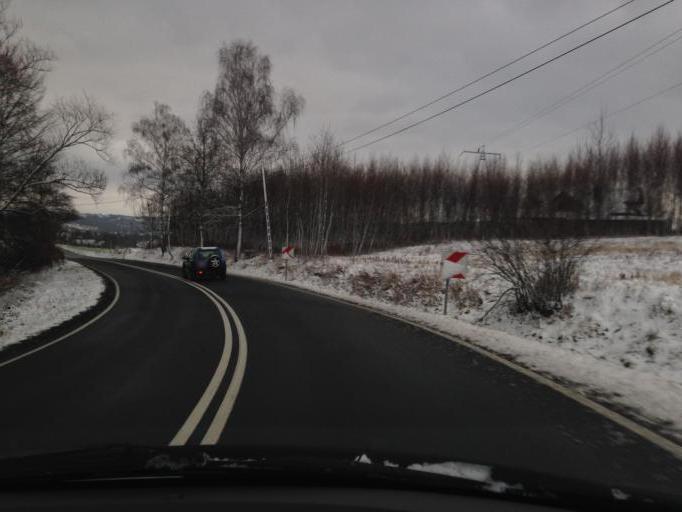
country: PL
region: Lesser Poland Voivodeship
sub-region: Powiat tarnowski
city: Gromnik
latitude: 49.8428
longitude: 20.9379
